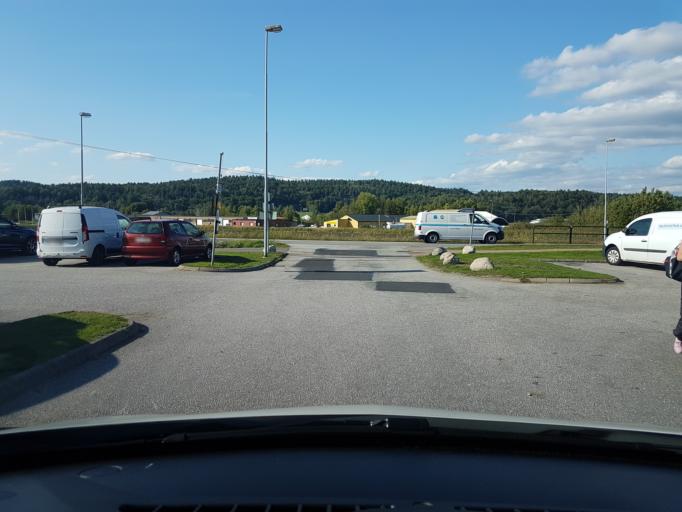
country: SE
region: Vaestra Goetaland
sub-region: Ale Kommun
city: Skepplanda
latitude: 57.9787
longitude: 12.1977
